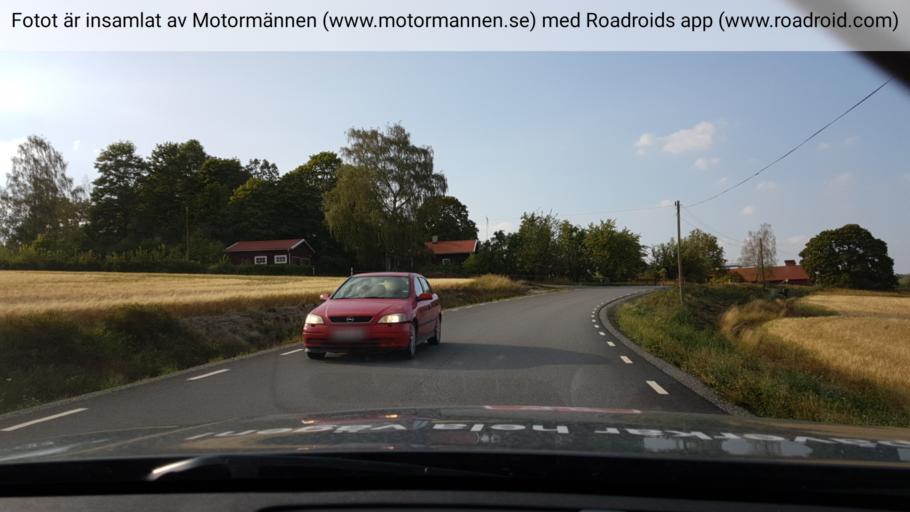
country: SE
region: Soedermanland
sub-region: Gnesta Kommun
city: Gnesta
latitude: 59.1260
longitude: 17.2146
